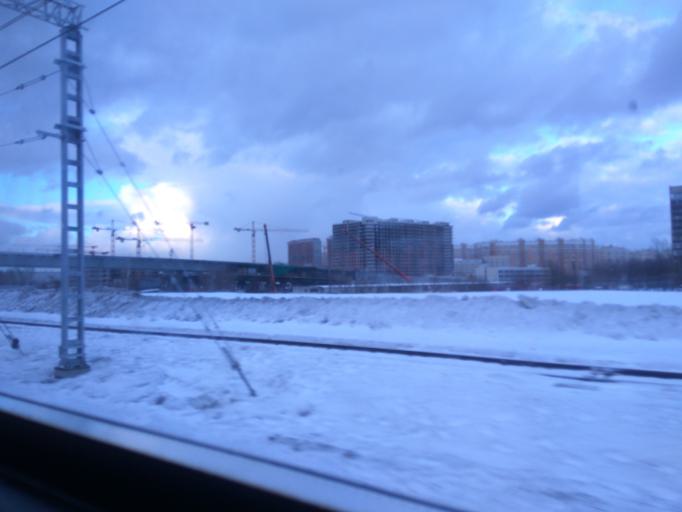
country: RU
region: Moskovskaya
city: Biryulevo Zapadnoye
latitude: 55.6003
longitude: 37.6498
